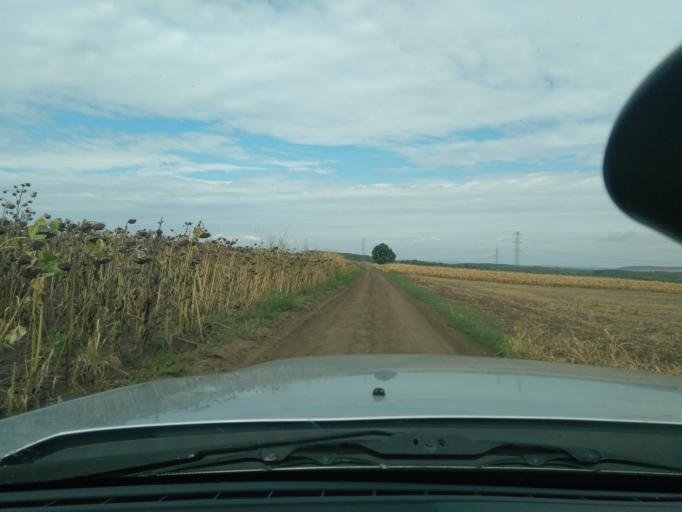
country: HU
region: Fejer
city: Val
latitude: 47.3686
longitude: 18.7002
